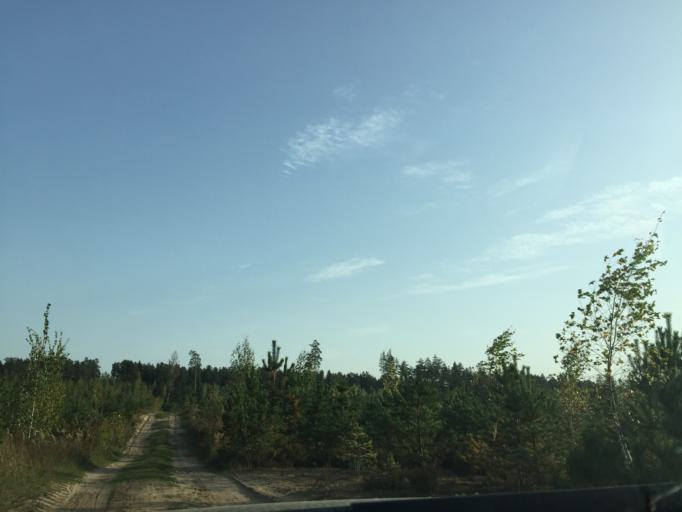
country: LV
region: Garkalne
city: Garkalne
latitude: 56.9690
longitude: 24.4200
